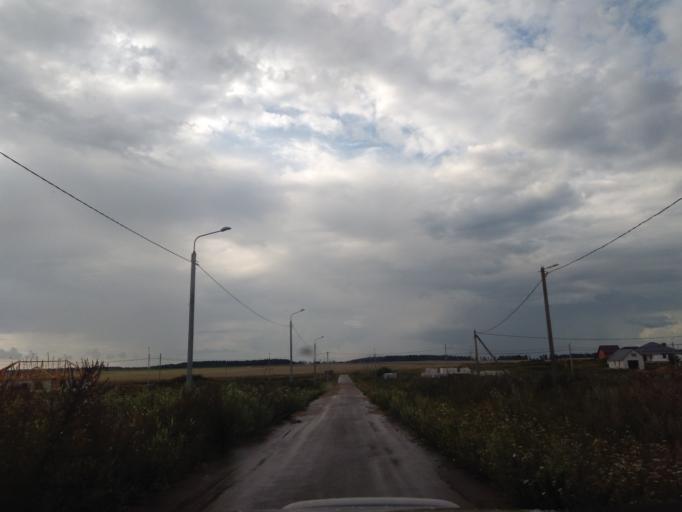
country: BY
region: Minsk
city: Kapyl'
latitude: 53.1616
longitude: 27.0780
